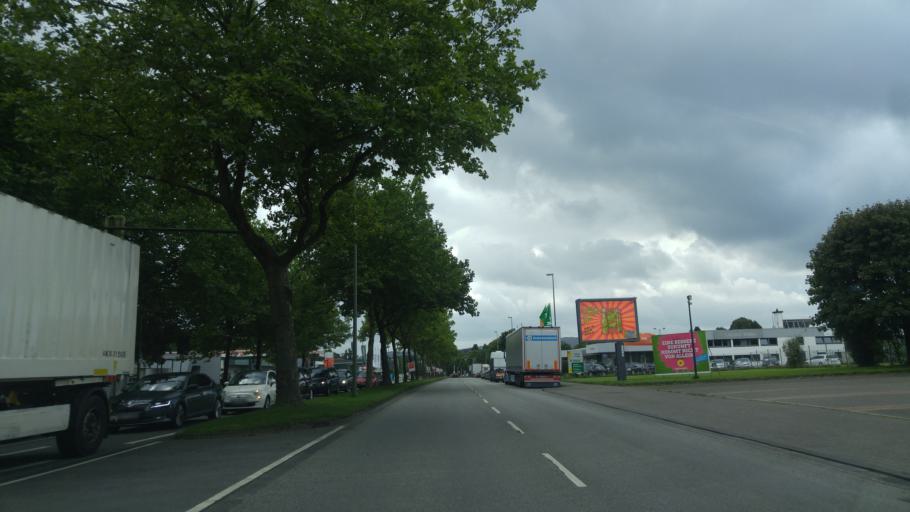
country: DE
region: North Rhine-Westphalia
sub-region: Regierungsbezirk Detmold
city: Bielefeld
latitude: 52.0578
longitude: 8.5194
